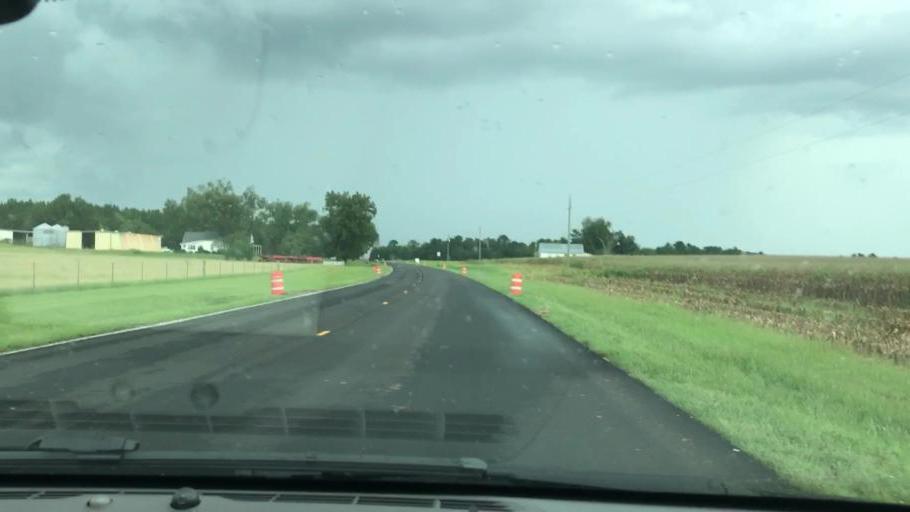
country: US
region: Georgia
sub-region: Clay County
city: Fort Gaines
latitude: 31.5023
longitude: -85.0186
